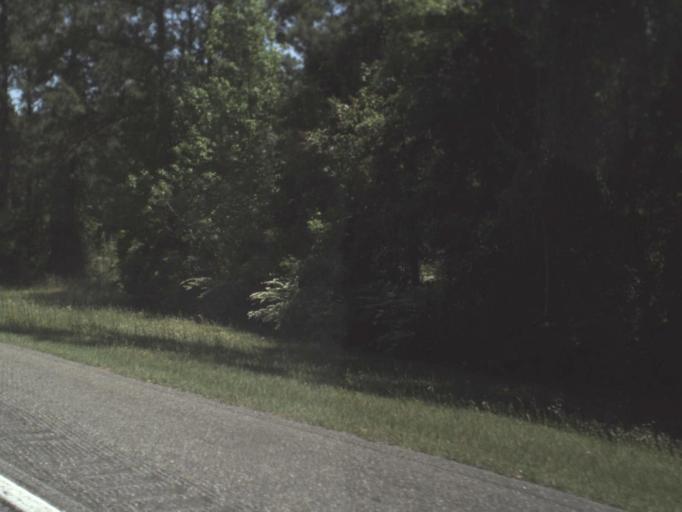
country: US
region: Florida
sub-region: Jefferson County
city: Monticello
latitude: 30.4874
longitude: -83.9610
